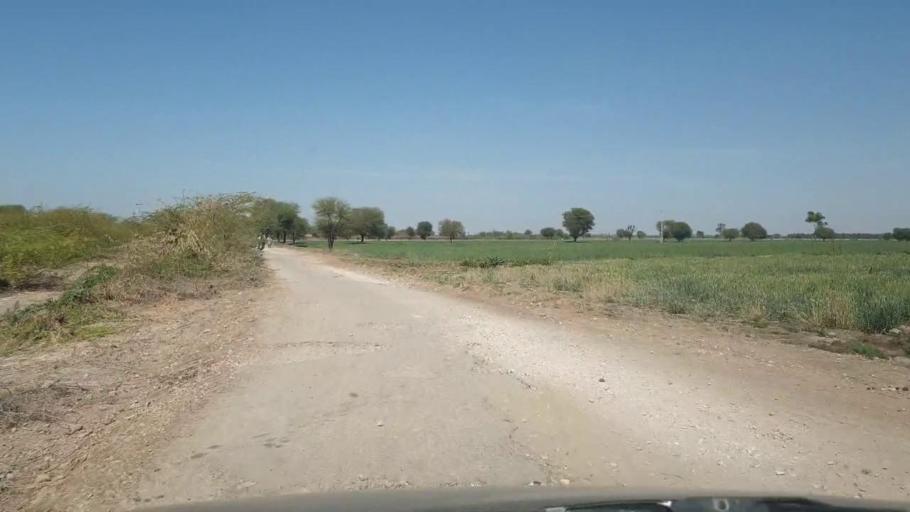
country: PK
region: Sindh
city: Dhoro Naro
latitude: 25.4680
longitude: 69.6070
